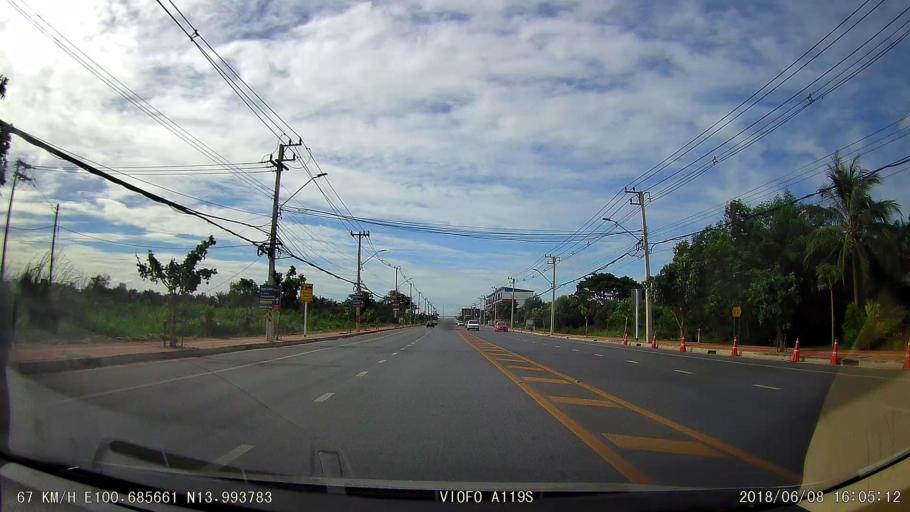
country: TH
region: Pathum Thani
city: Thanyaburi
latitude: 13.9940
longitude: 100.6857
